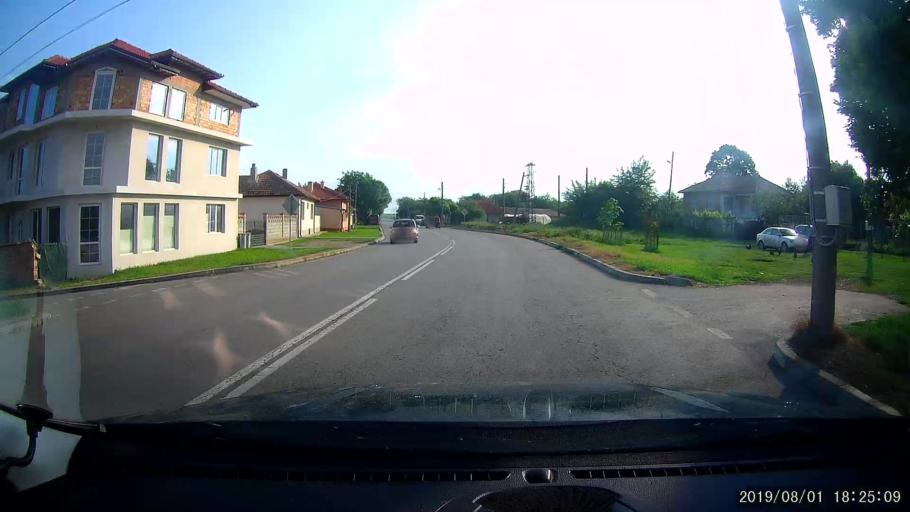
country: BG
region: Shumen
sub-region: Obshtina Venets
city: Venets
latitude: 43.6191
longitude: 26.9990
